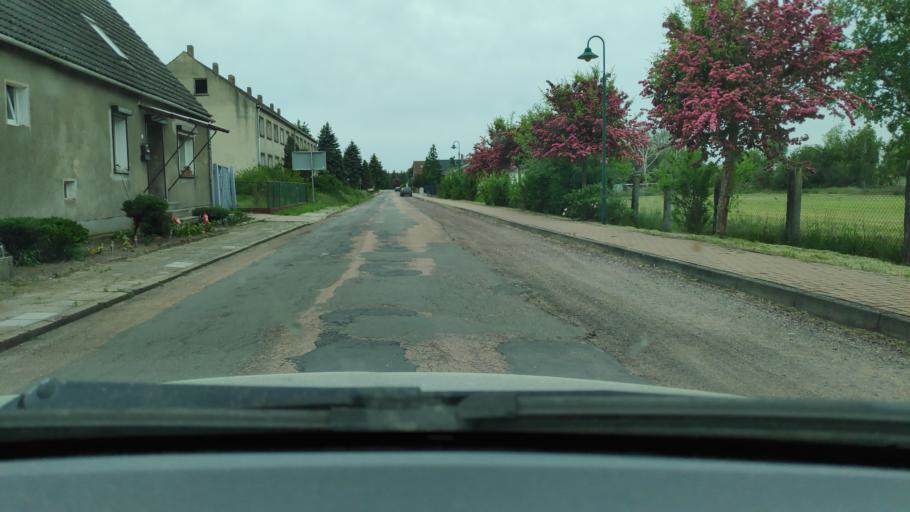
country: DE
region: Saxony-Anhalt
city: Leitzkau
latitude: 52.0135
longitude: 12.0139
